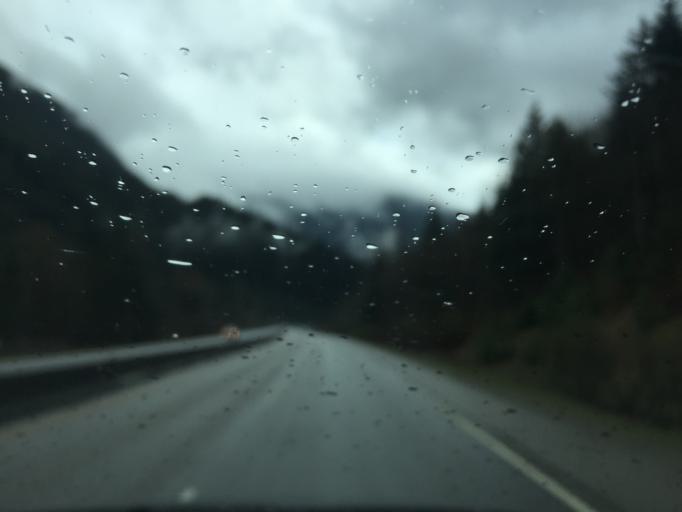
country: CA
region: British Columbia
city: Hope
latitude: 49.4083
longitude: -121.3176
